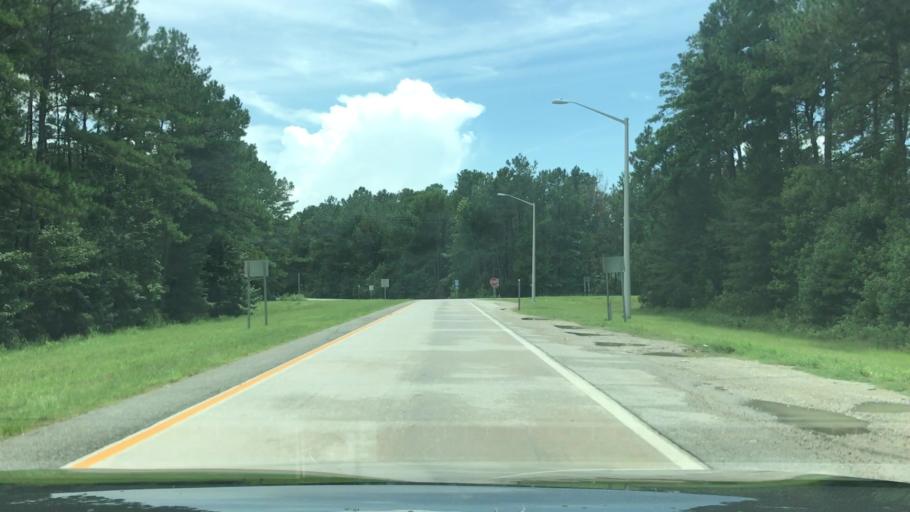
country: US
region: South Carolina
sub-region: Colleton County
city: Walterboro
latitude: 33.0039
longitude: -80.6702
